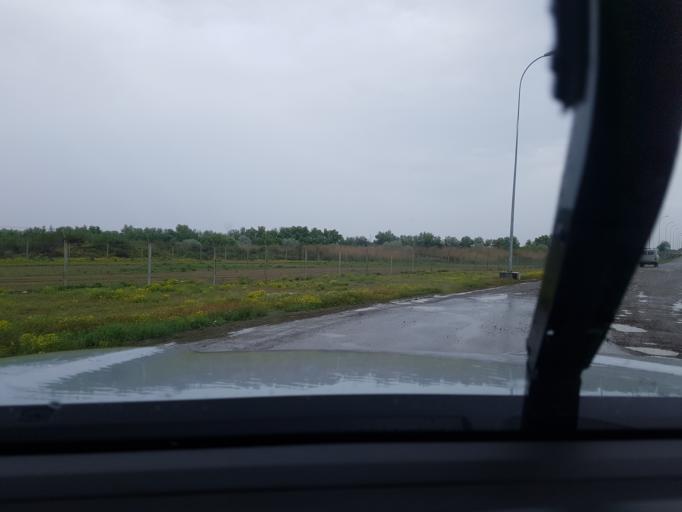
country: TM
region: Lebap
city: Farap
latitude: 39.2165
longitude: 63.7126
